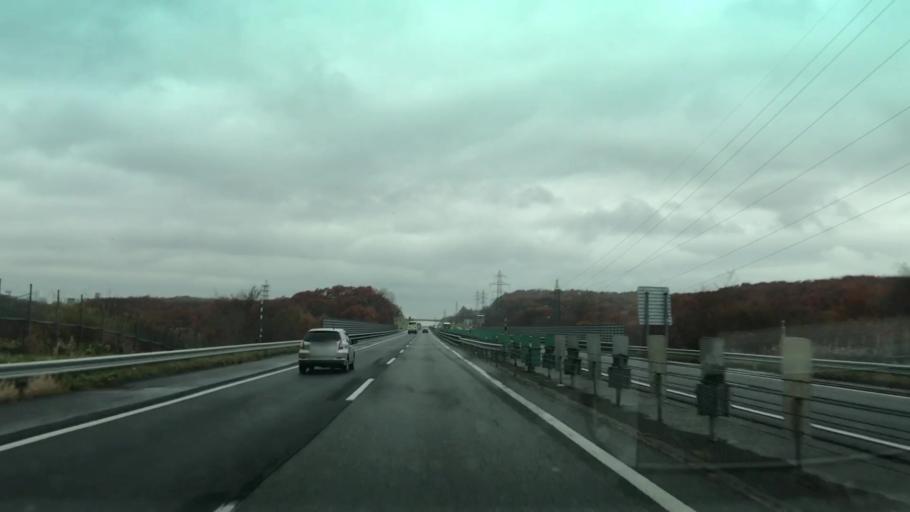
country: JP
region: Hokkaido
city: Kitahiroshima
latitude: 42.9570
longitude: 141.5051
